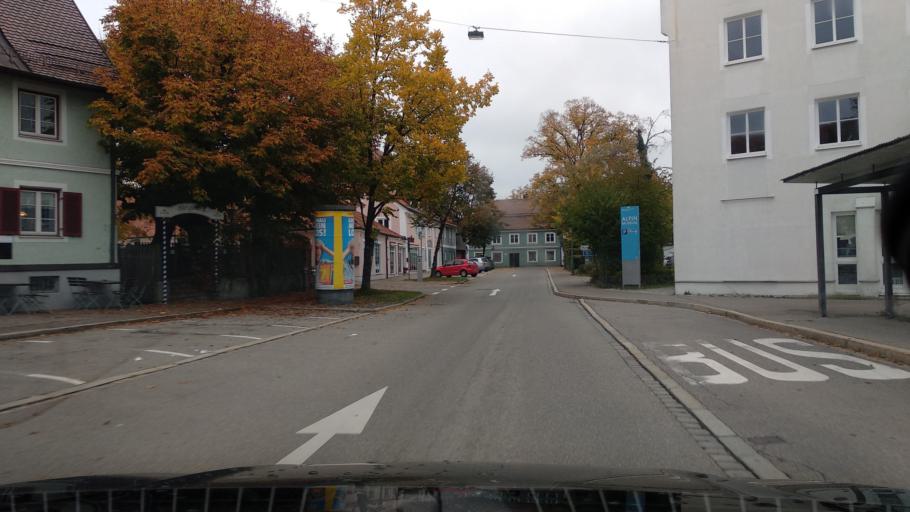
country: DE
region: Bavaria
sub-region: Swabia
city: Kempten (Allgaeu)
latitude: 47.7294
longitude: 10.3105
